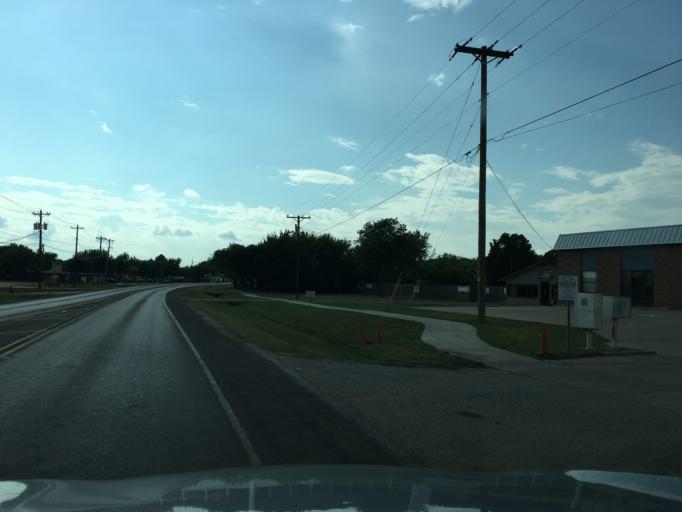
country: US
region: Texas
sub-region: Denton County
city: Denton
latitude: 33.2106
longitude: -97.0843
